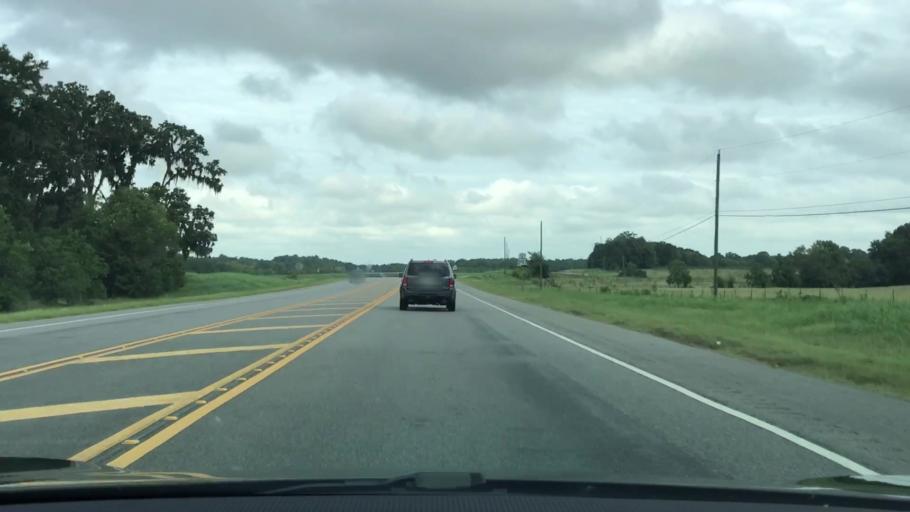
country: US
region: Alabama
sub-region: Montgomery County
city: Pike Road
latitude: 32.3327
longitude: -86.0573
